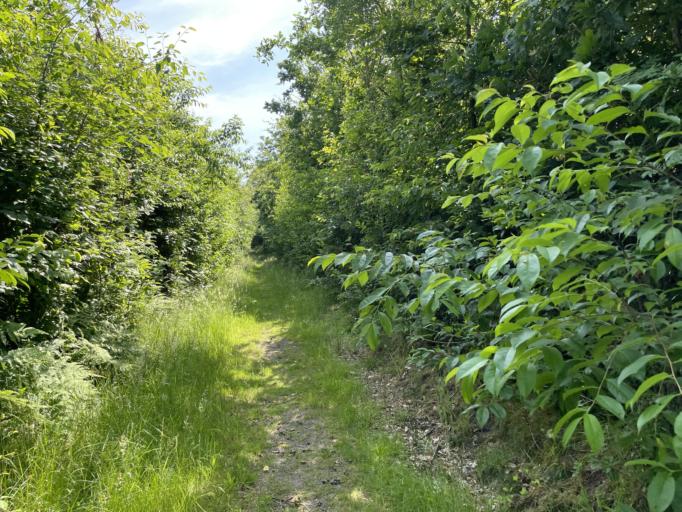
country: DE
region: Schleswig-Holstein
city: Mildstedt
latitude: 54.4708
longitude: 9.1039
